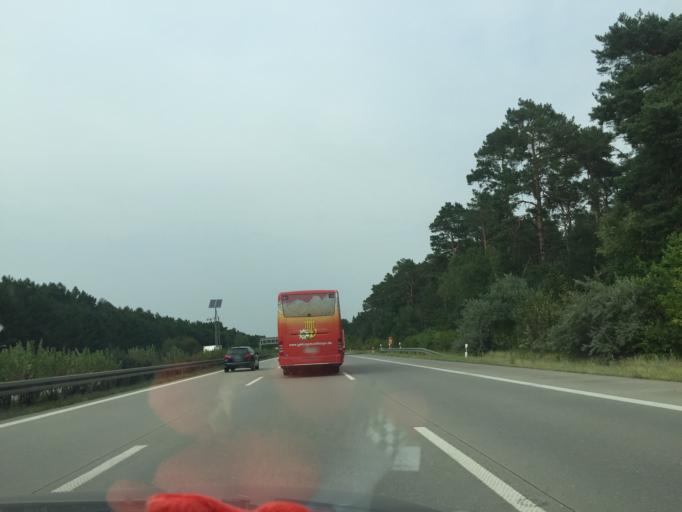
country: DE
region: Brandenburg
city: Erkner
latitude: 52.3383
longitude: 13.7536
